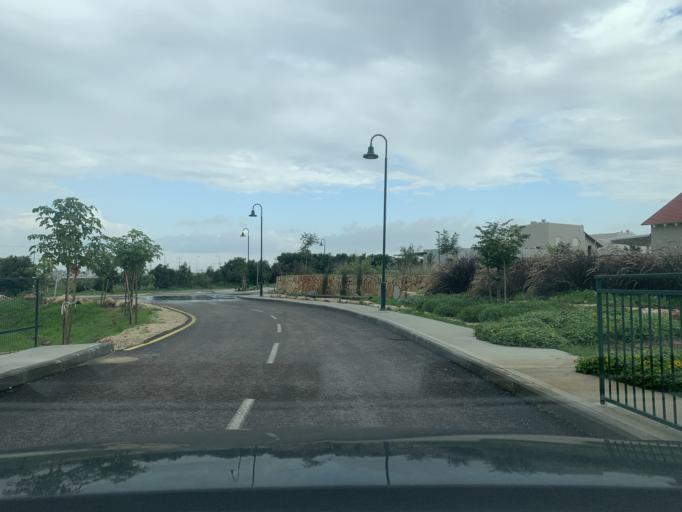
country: PS
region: West Bank
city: Qalqilyah
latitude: 32.2127
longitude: 34.9769
